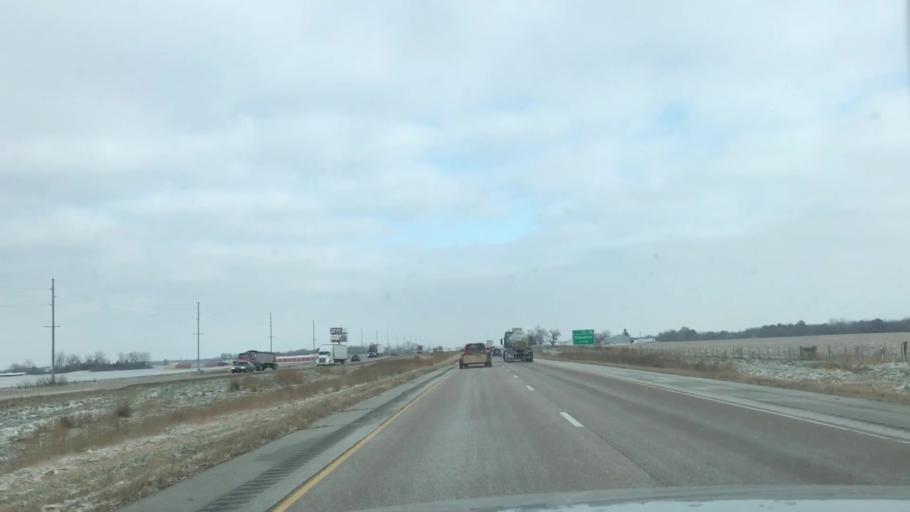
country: US
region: Illinois
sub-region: Macoupin County
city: Staunton
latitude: 38.9997
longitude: -89.7496
